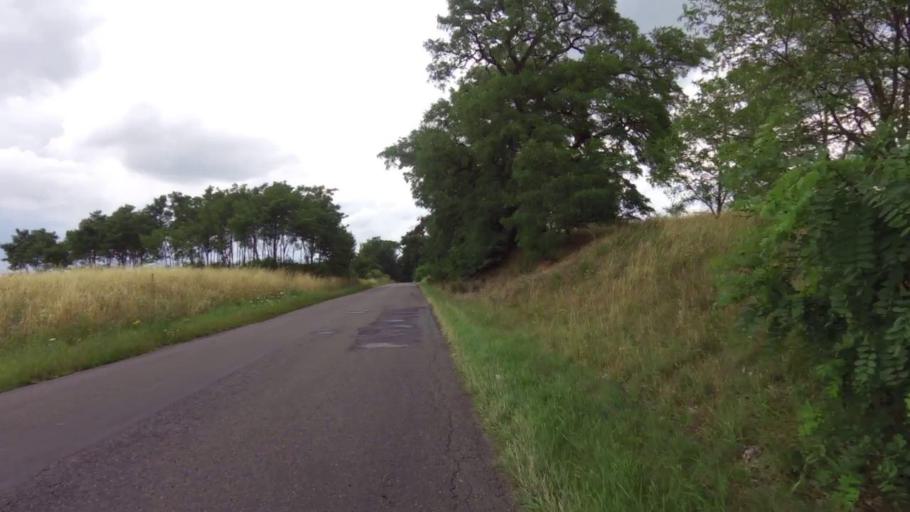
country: PL
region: West Pomeranian Voivodeship
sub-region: Powiat gryfinski
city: Moryn
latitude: 52.8645
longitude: 14.3857
